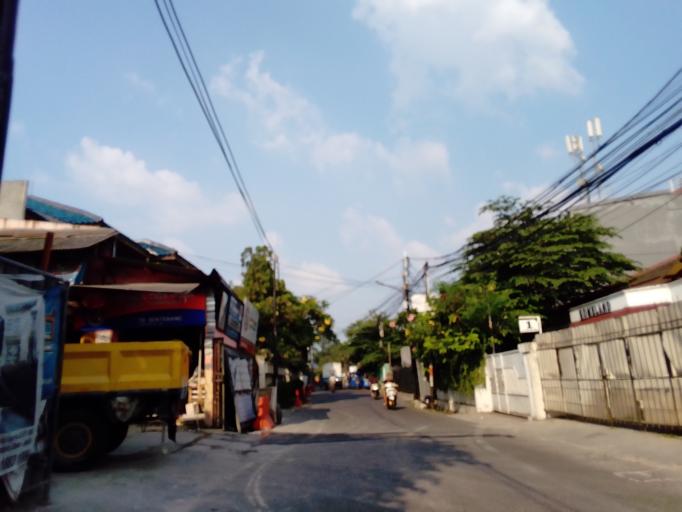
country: ID
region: Jakarta Raya
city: Jakarta
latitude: -6.2609
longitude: 106.7925
